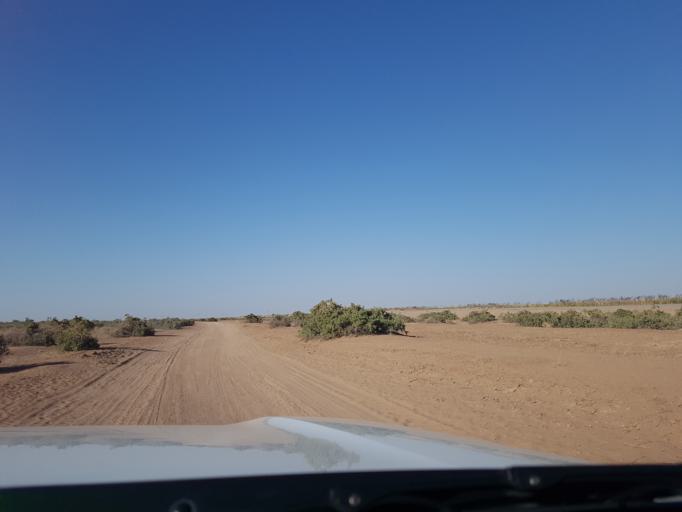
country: IR
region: Razavi Khorasan
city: Sarakhs
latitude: 36.9920
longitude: 61.3881
